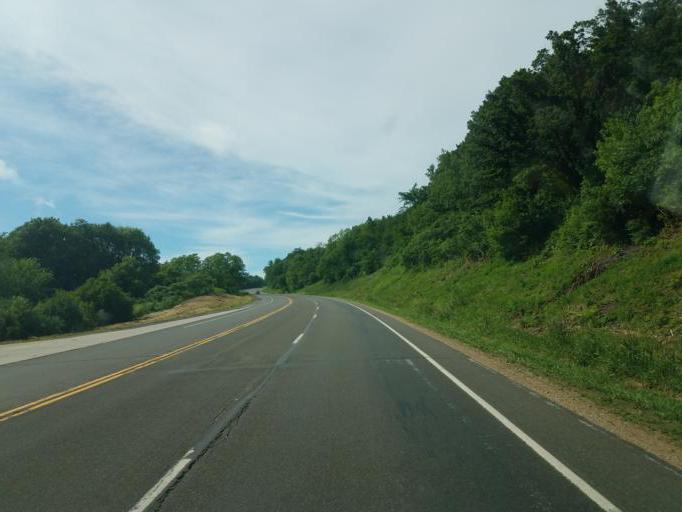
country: US
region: Wisconsin
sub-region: Monroe County
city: Tomah
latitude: 43.8878
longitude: -90.4815
